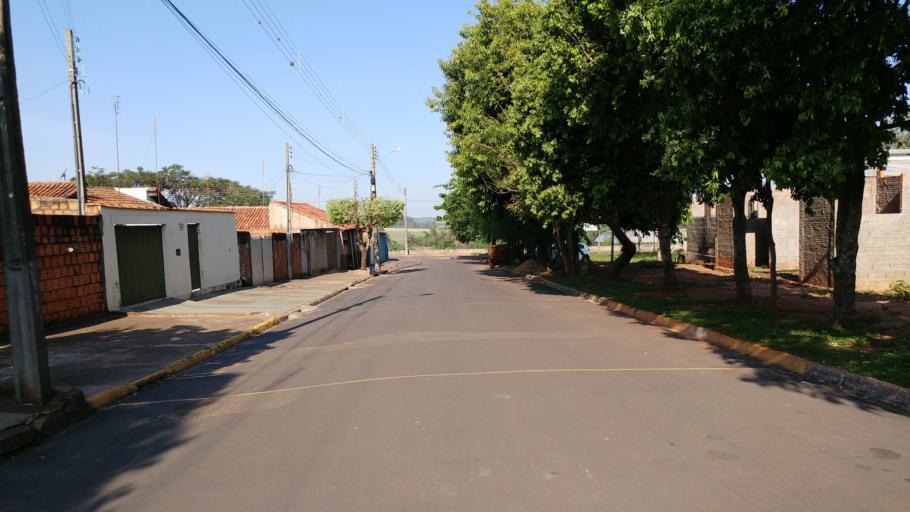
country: BR
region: Sao Paulo
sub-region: Paraguacu Paulista
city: Paraguacu Paulista
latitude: -22.4196
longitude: -50.5689
